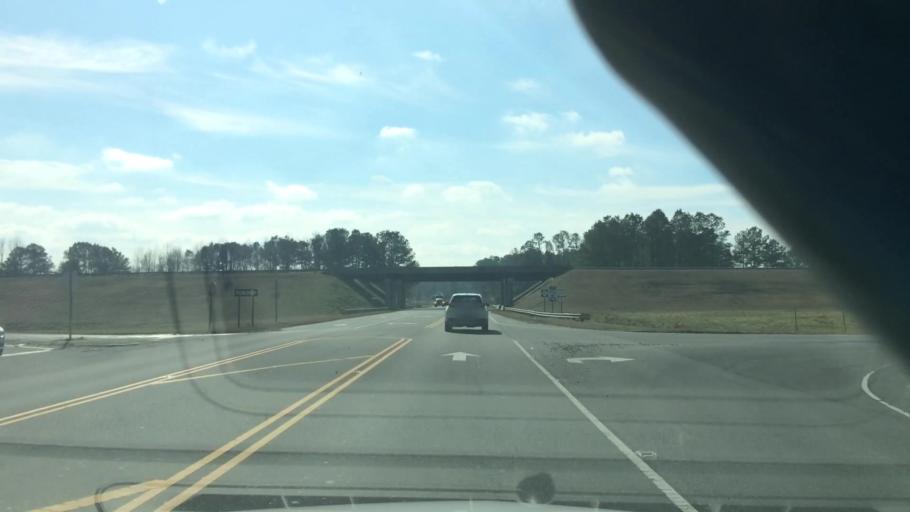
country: US
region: North Carolina
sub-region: Duplin County
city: Wallace
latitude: 34.7562
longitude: -77.9497
